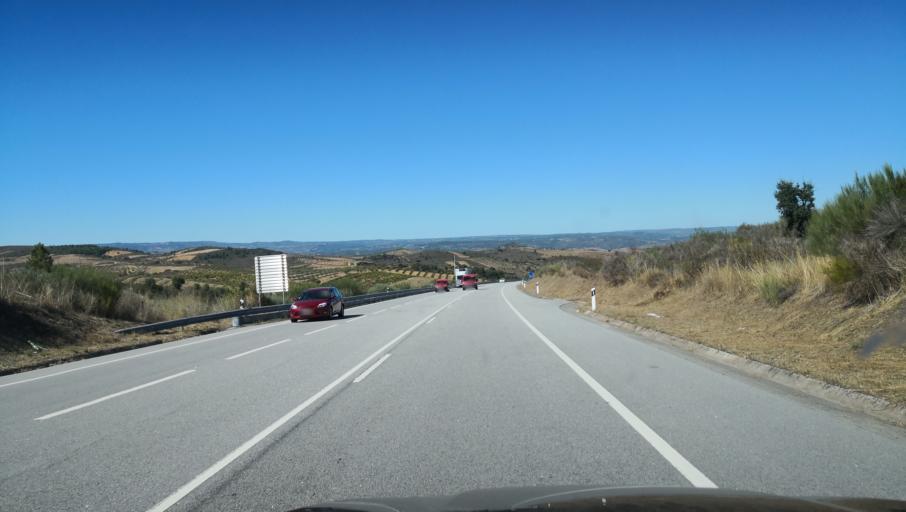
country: PT
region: Braganca
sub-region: Mirandela
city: Mirandela
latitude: 41.4929
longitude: -7.2272
